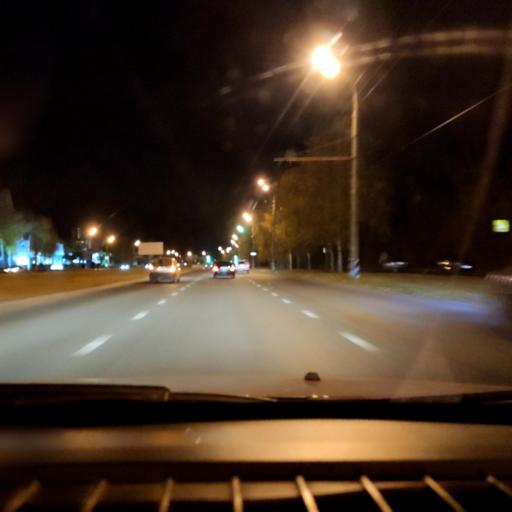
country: RU
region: Samara
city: Tol'yatti
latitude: 53.5028
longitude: 49.2602
